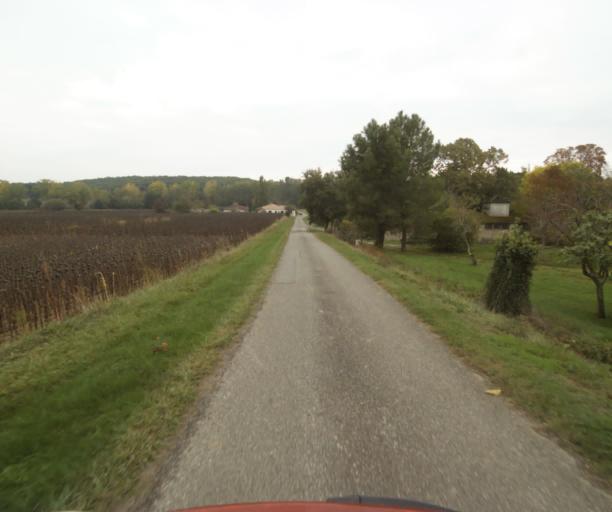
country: FR
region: Midi-Pyrenees
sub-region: Departement de la Haute-Garonne
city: Grenade
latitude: 43.7802
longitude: 1.2298
